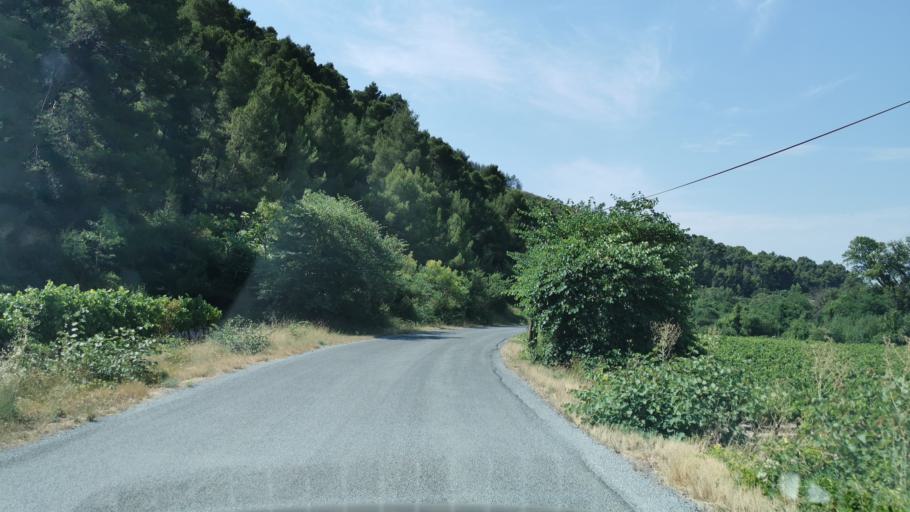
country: FR
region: Languedoc-Roussillon
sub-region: Departement de l'Aude
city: Bize-Minervois
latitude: 43.3207
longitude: 2.8810
